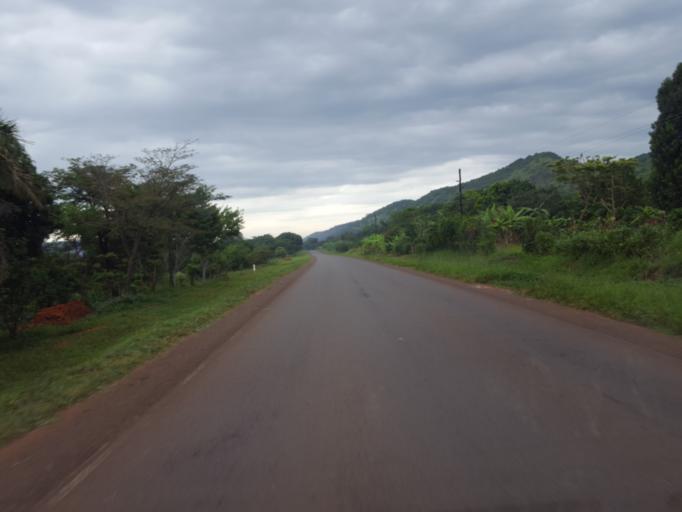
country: UG
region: Central Region
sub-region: Kiboga District
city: Kiboga
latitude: 0.8483
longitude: 31.8742
